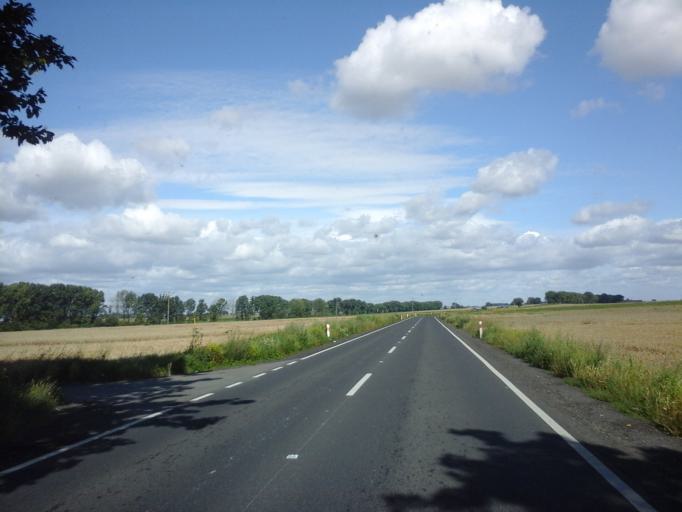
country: PL
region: West Pomeranian Voivodeship
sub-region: Powiat stargardzki
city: Dolice
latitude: 53.2418
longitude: 15.1084
